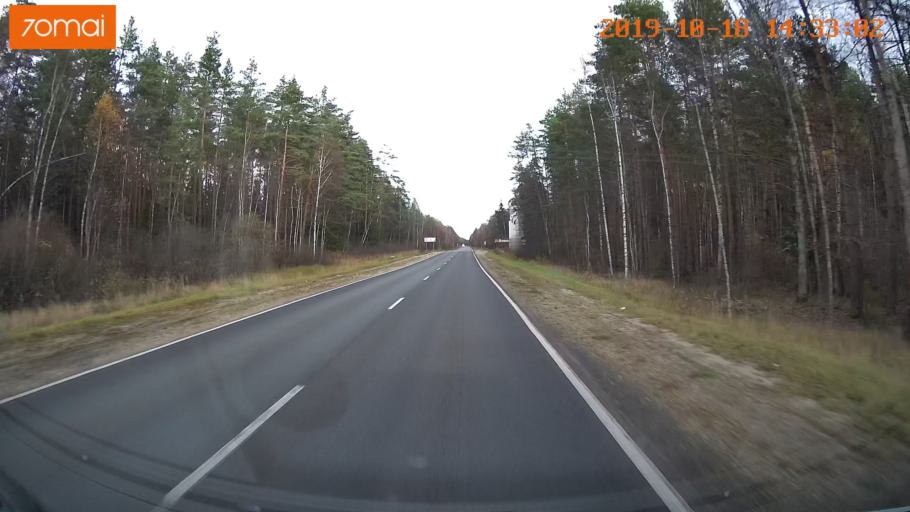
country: RU
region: Rjazan
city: Tuma
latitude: 55.1970
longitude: 40.5895
